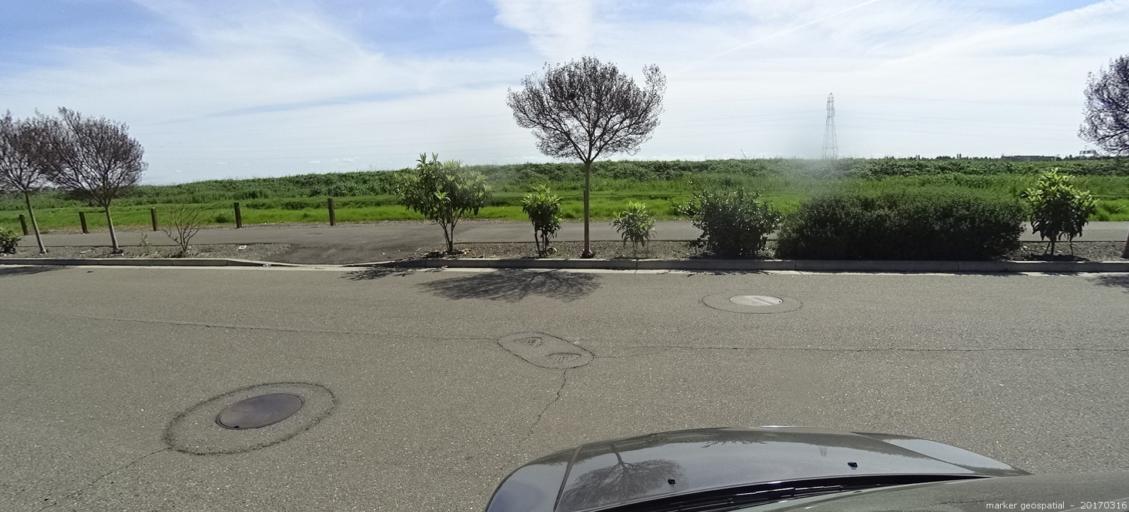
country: US
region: California
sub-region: Sacramento County
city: Parkway
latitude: 38.4719
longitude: -121.4915
